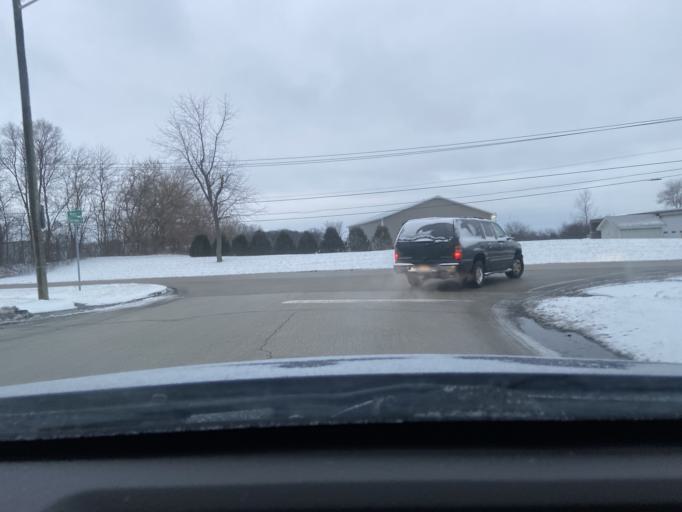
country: US
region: Illinois
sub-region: Lake County
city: Round Lake Park
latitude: 42.3484
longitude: -88.0769
